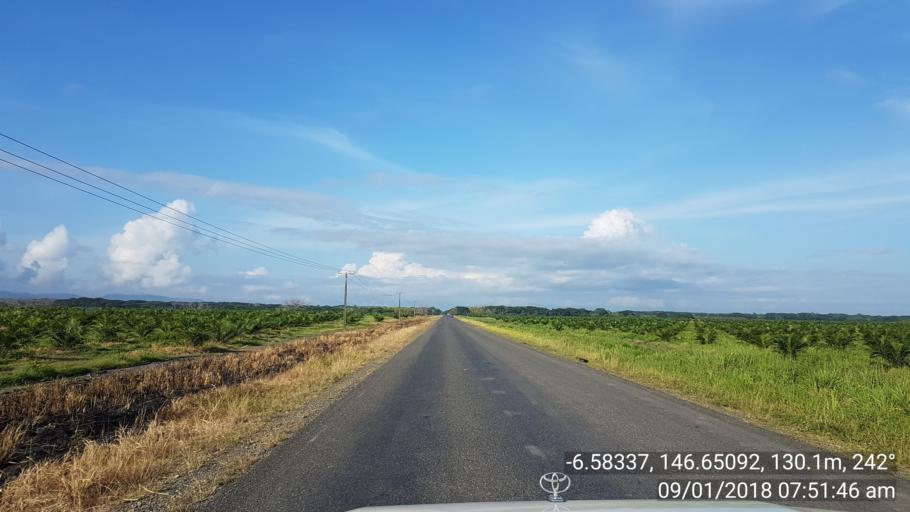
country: PG
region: Morobe
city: Lae
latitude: -6.5833
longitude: 146.6511
